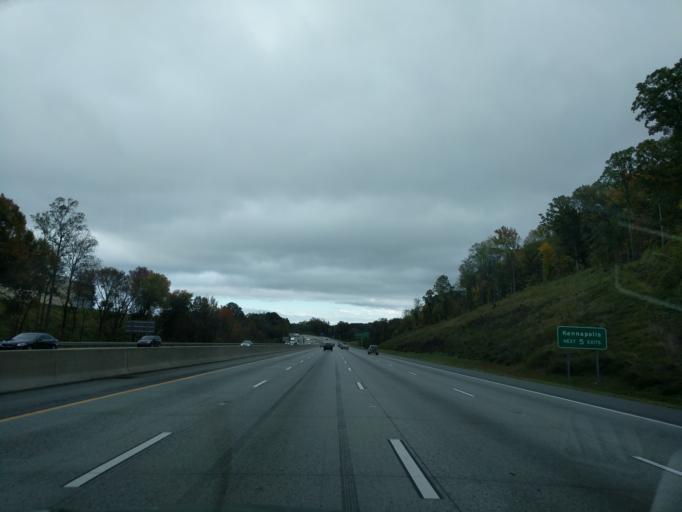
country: US
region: North Carolina
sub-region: Cabarrus County
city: Harrisburg
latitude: 35.4093
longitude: -80.6890
